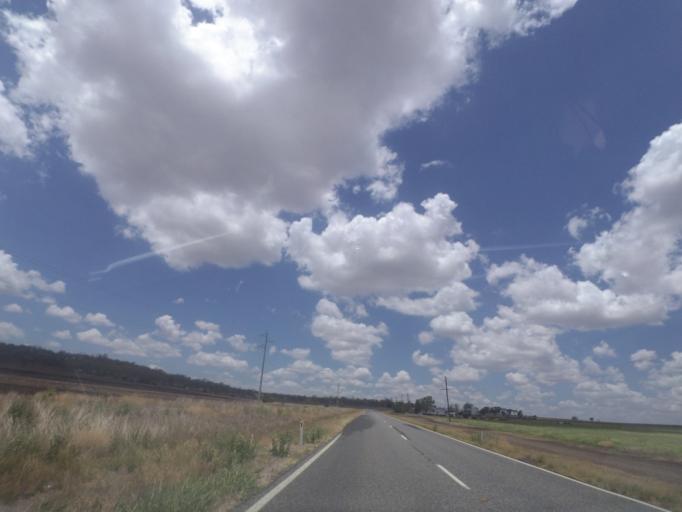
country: AU
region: Queensland
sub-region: Toowoomba
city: Top Camp
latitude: -27.8753
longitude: 151.9655
